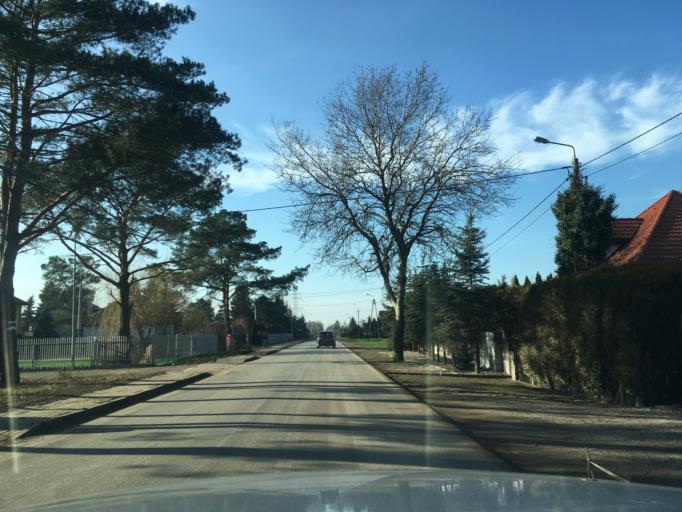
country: PL
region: Masovian Voivodeship
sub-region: Powiat piaseczynski
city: Lesznowola
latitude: 52.0560
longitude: 20.8851
